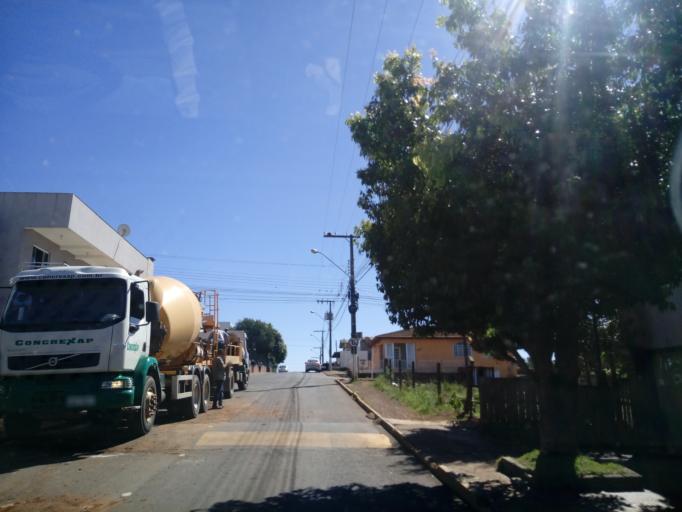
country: BR
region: Santa Catarina
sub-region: Chapeco
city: Chapeco
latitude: -27.0940
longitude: -52.6739
